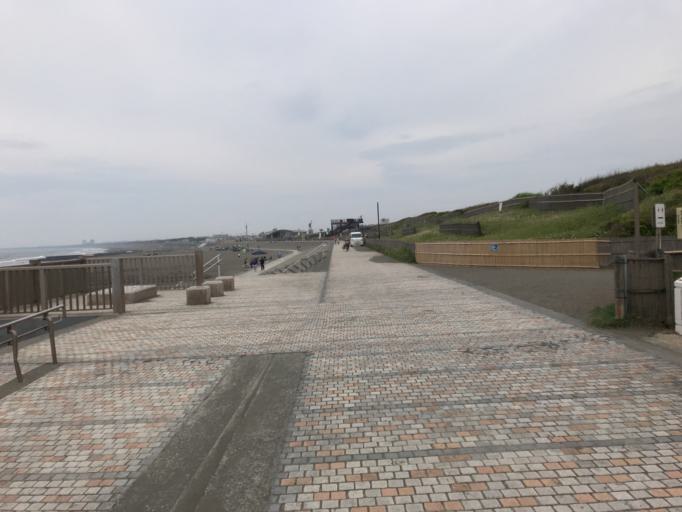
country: JP
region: Kanagawa
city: Fujisawa
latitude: 35.3142
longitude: 139.4732
